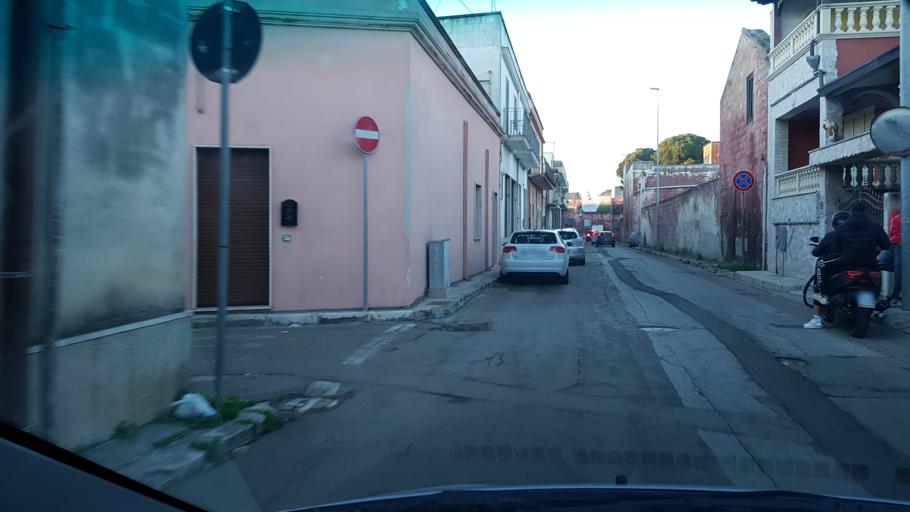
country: IT
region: Apulia
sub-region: Provincia di Brindisi
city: San Pietro Vernotico
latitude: 40.4866
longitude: 18.0009
